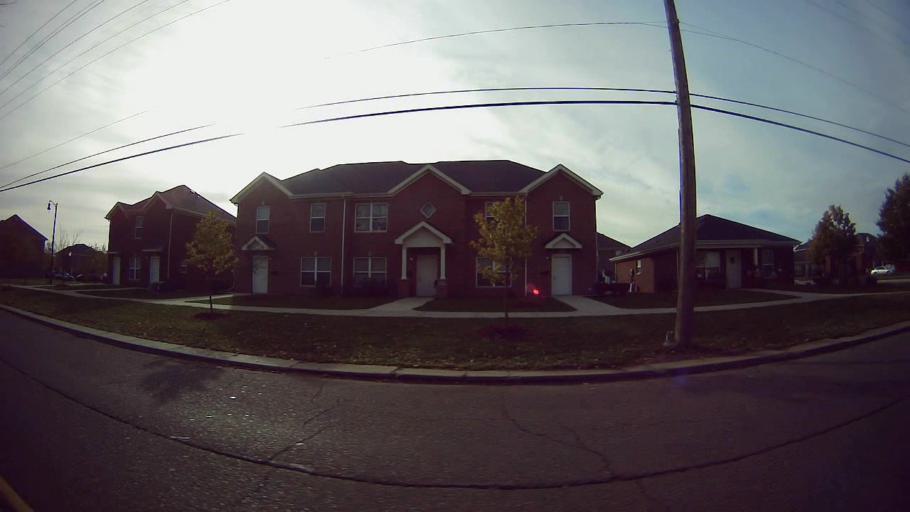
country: US
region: Michigan
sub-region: Wayne County
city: Hamtramck
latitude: 42.4117
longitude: -83.0512
